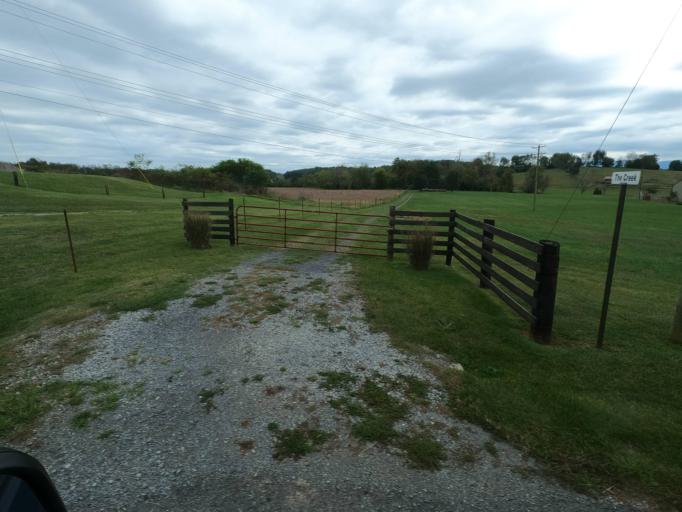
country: US
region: Tennessee
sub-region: Washington County
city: Jonesborough
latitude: 36.2323
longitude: -82.5821
